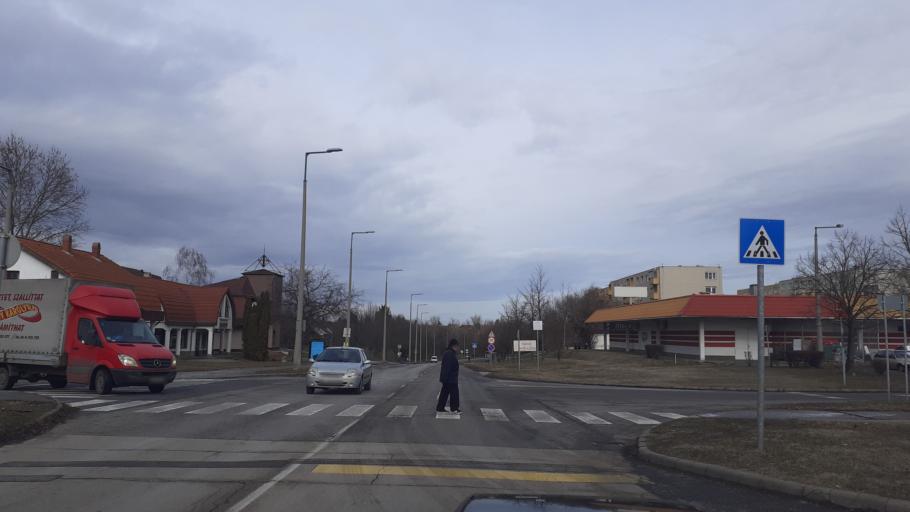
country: HU
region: Fejer
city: dunaujvaros
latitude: 46.9658
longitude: 18.9159
